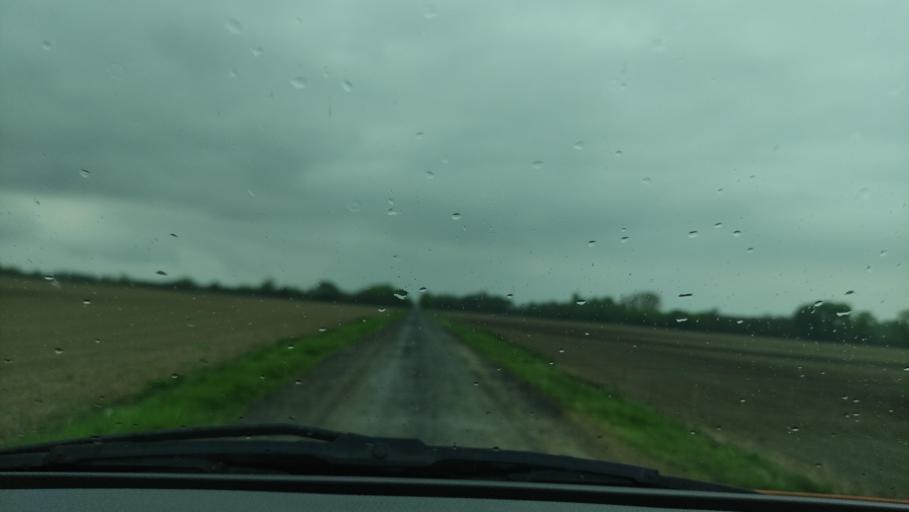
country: HR
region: Osjecko-Baranjska
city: Batina
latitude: 45.8954
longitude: 18.7896
